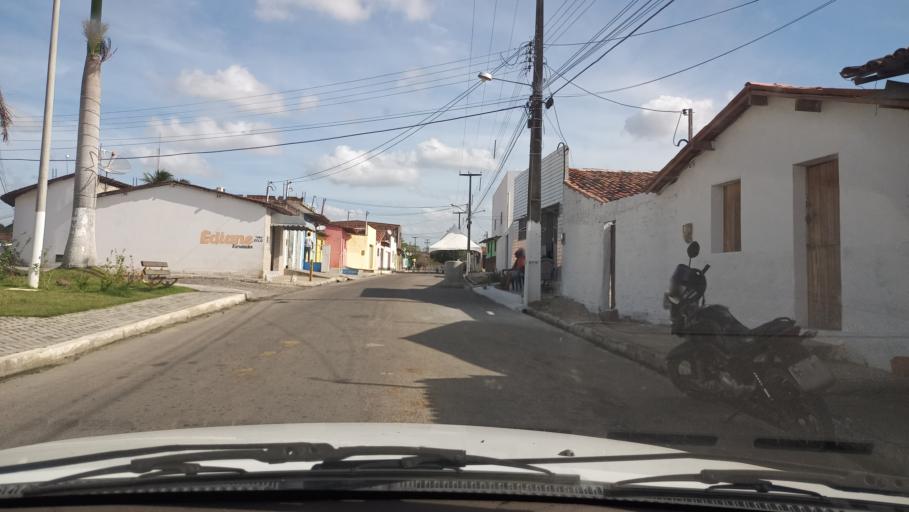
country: BR
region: Rio Grande do Norte
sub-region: Goianinha
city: Goianinha
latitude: -6.3343
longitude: -35.3009
